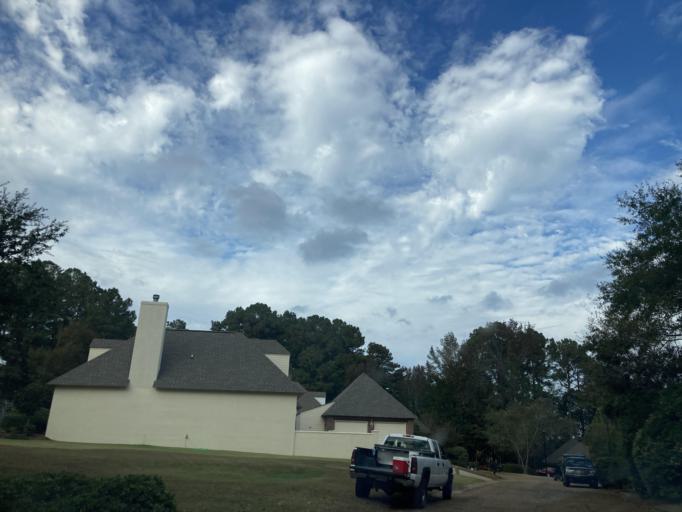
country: US
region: Mississippi
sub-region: Lamar County
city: West Hattiesburg
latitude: 31.3157
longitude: -89.4659
